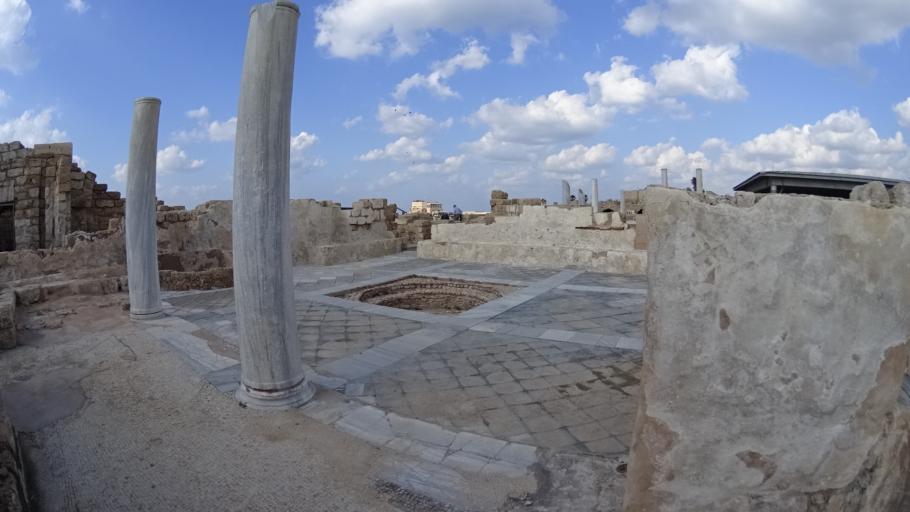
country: IL
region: Haifa
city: Qesarya
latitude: 32.4990
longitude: 34.8913
